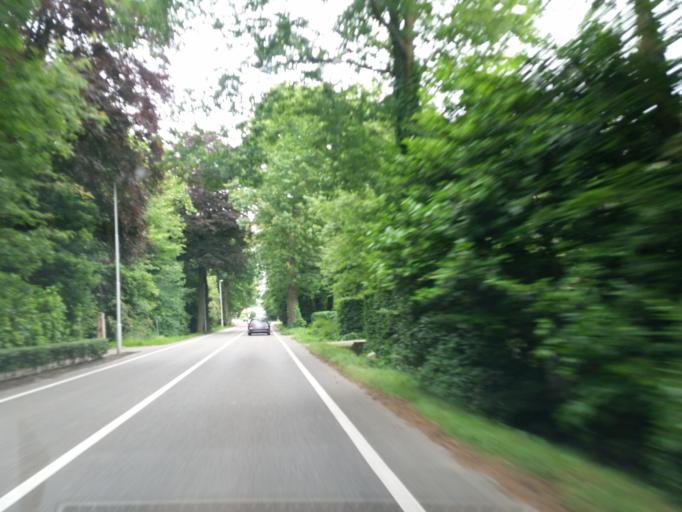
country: BE
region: Flanders
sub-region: Provincie Antwerpen
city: Schoten
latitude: 51.2651
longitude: 4.5434
